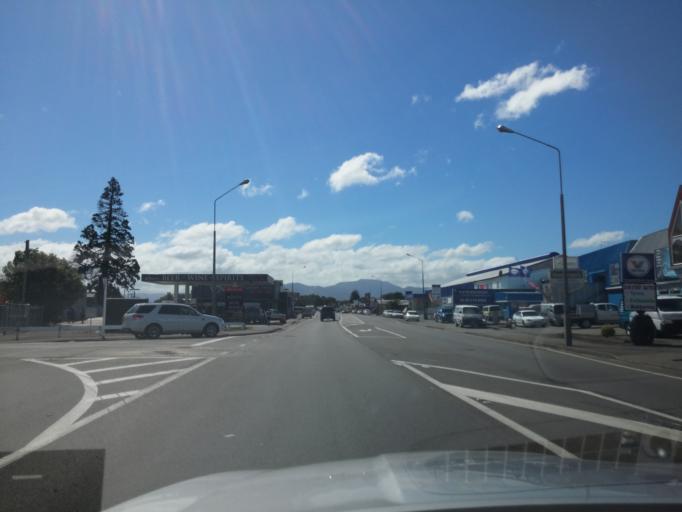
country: NZ
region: Marlborough
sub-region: Marlborough District
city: Blenheim
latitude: -41.5063
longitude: 173.9596
